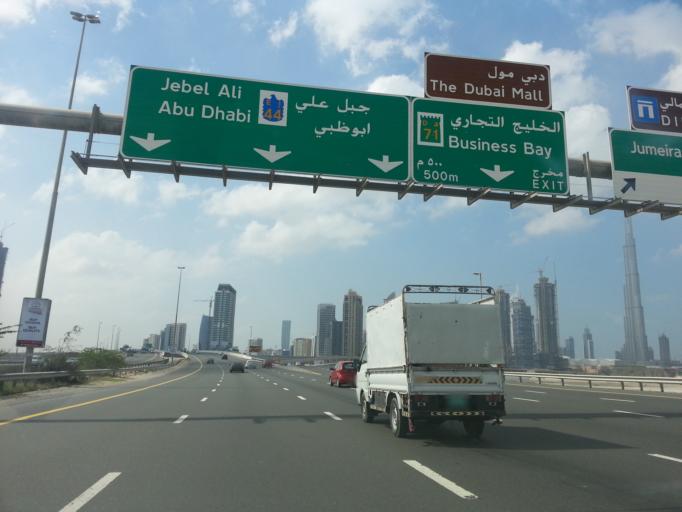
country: AE
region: Ash Shariqah
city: Sharjah
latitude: 25.1977
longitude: 55.2988
